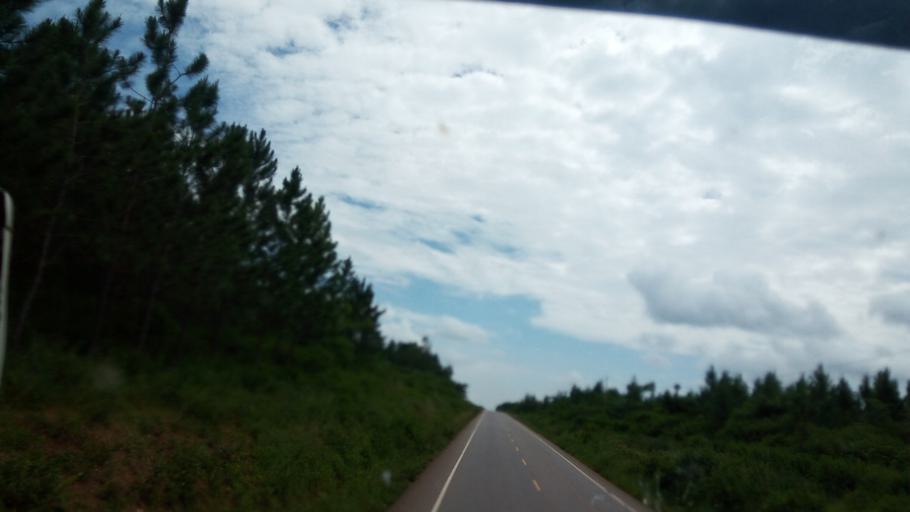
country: UG
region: Central Region
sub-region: Nakasongola District
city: Nakasongola
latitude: 1.1347
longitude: 32.4651
